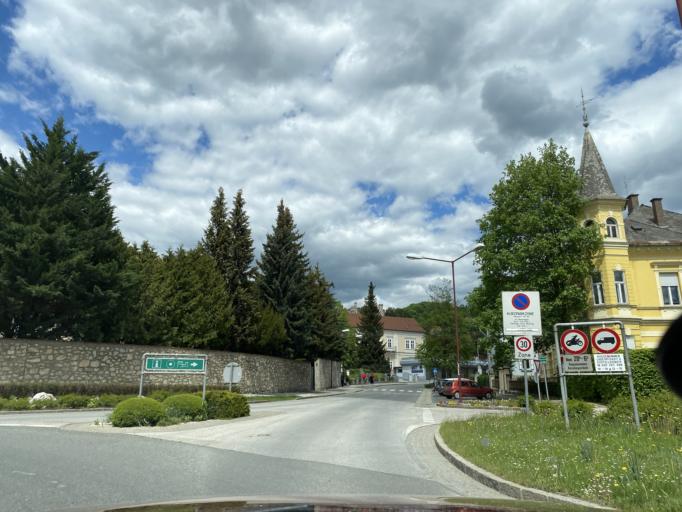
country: AT
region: Carinthia
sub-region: Politischer Bezirk Wolfsberg
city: Wolfsberg
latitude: 46.8357
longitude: 14.8442
